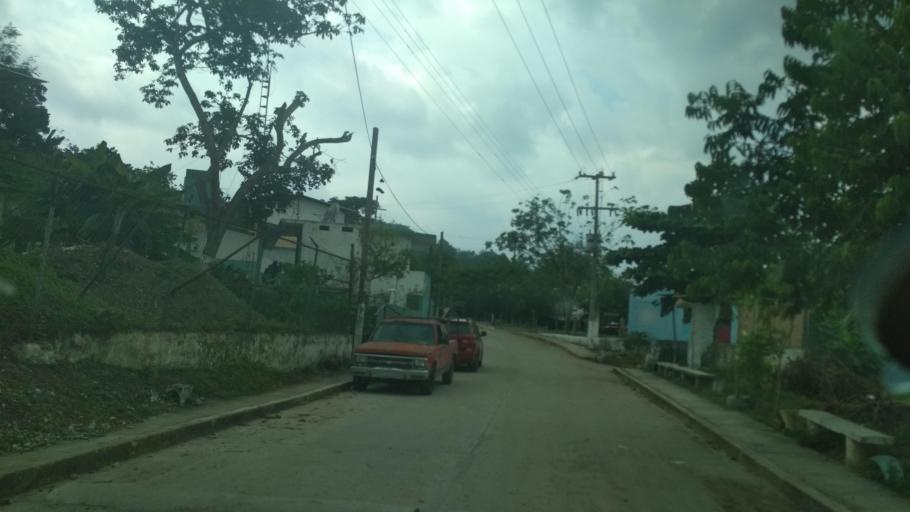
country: MX
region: Veracruz
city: Papantla de Olarte
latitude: 20.4788
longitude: -97.3561
